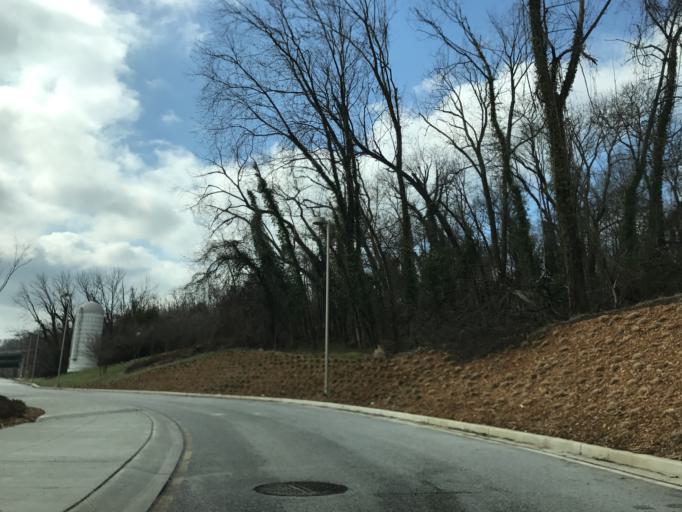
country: US
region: Maryland
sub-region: Baltimore County
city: Arbutus
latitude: 39.2489
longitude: -76.7159
